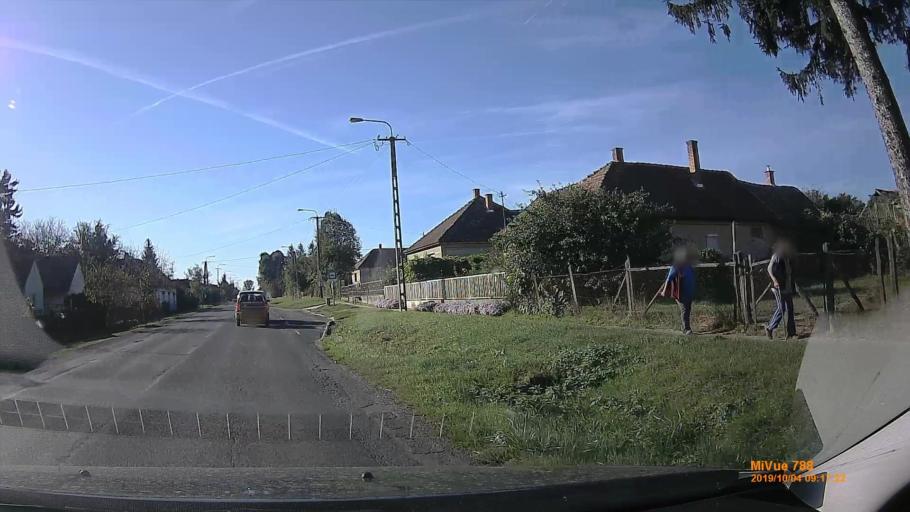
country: HU
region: Somogy
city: Karad
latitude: 46.6028
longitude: 17.7998
